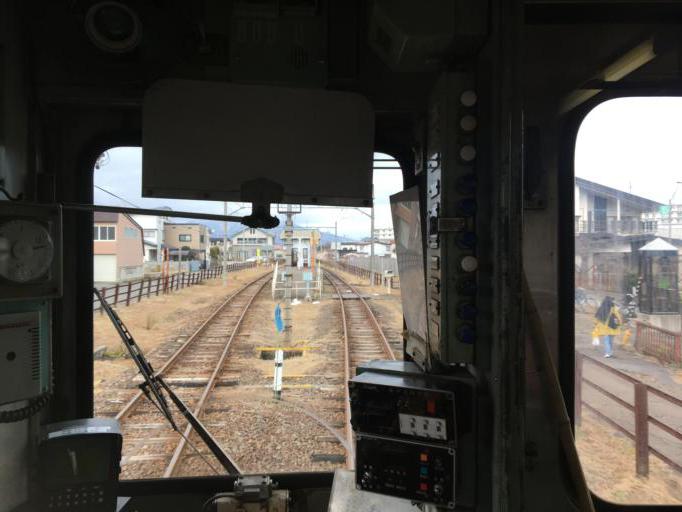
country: JP
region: Aomori
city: Hirosaki
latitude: 40.5669
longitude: 140.4810
